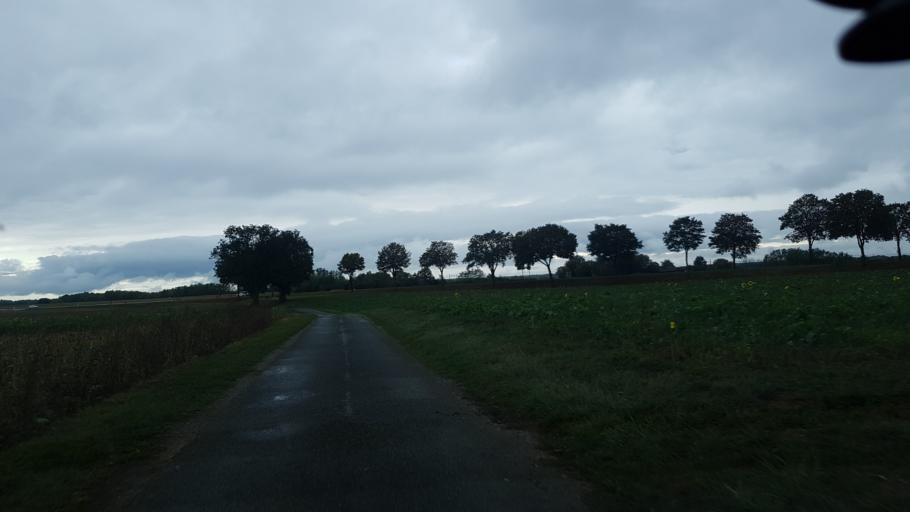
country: FR
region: Rhone-Alpes
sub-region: Departement de l'Ain
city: Tossiat
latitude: 46.1219
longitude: 5.2979
